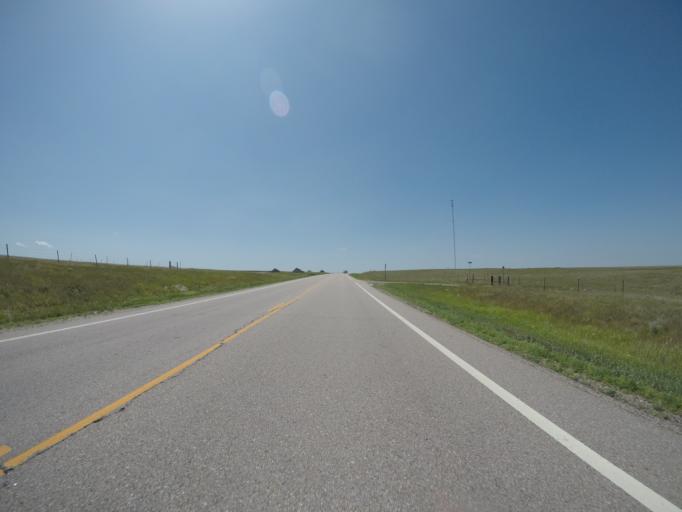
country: US
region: Kansas
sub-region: Osborne County
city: Osborne
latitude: 39.4814
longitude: -98.6950
